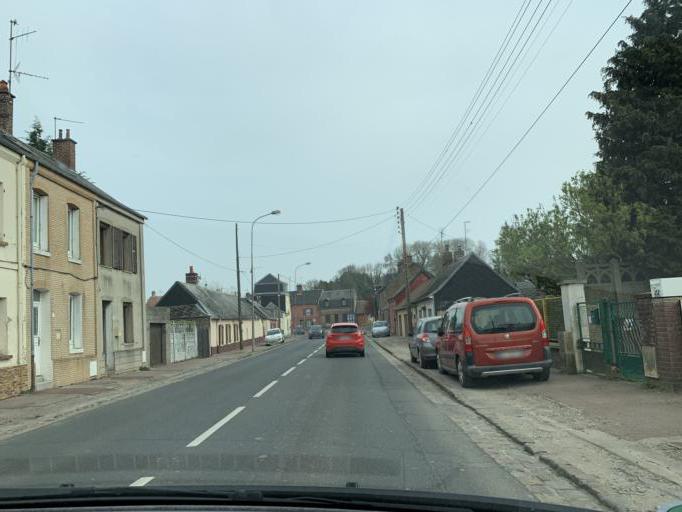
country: FR
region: Picardie
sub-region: Departement de la Somme
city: Abbeville
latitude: 50.1051
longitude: 1.7971
